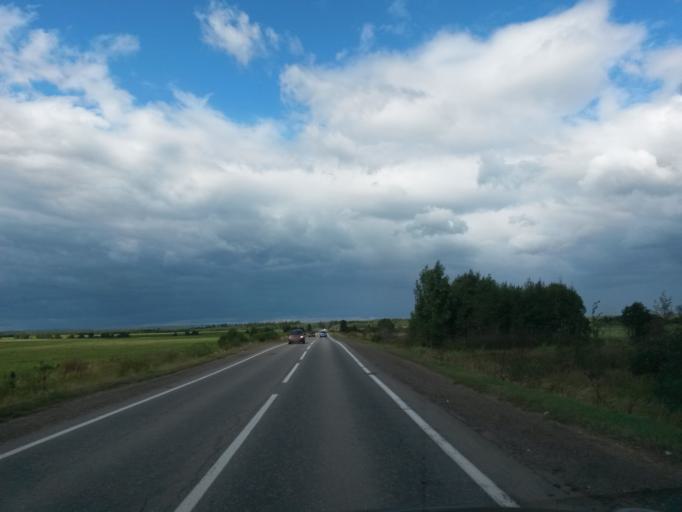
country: RU
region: Jaroslavl
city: Yaroslavl
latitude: 57.7724
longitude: 39.8536
